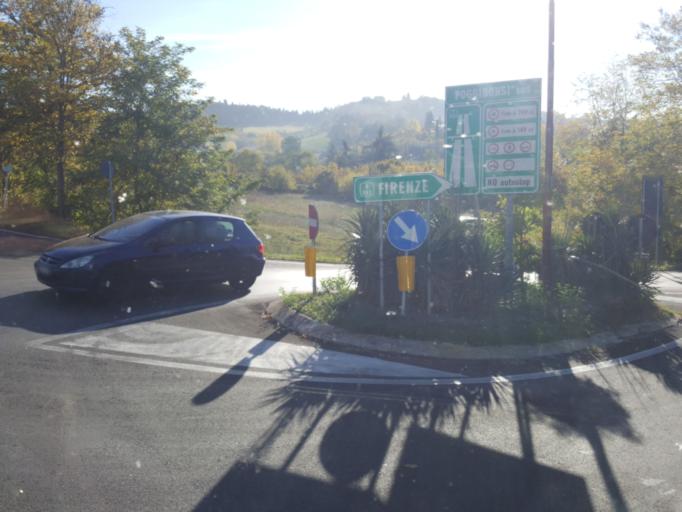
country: IT
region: Tuscany
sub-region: Provincia di Siena
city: Poggibonsi
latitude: 43.4686
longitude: 11.1582
